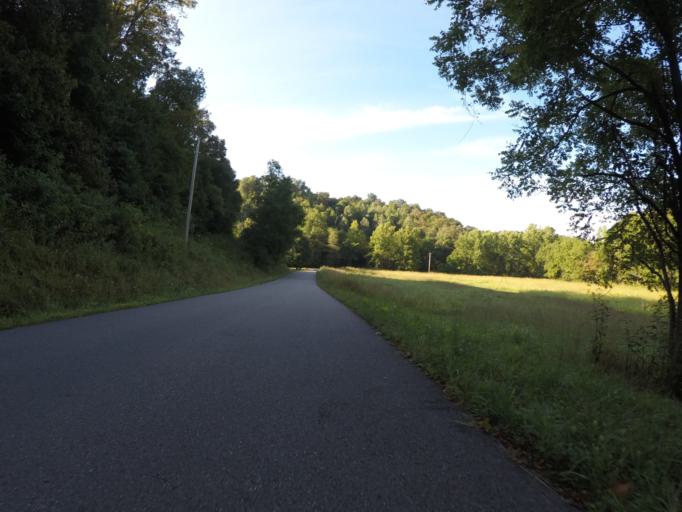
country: US
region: Ohio
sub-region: Lawrence County
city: Coal Grove
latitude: 38.5552
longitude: -82.5537
